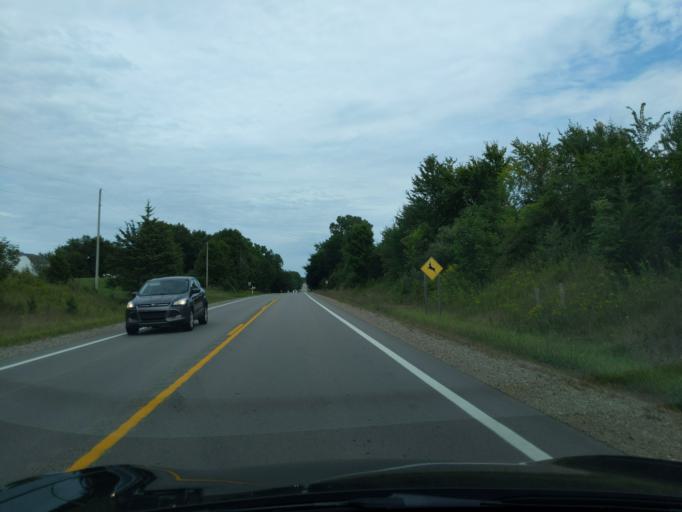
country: US
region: Michigan
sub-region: Barry County
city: Nashville
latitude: 42.5674
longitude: -85.0215
